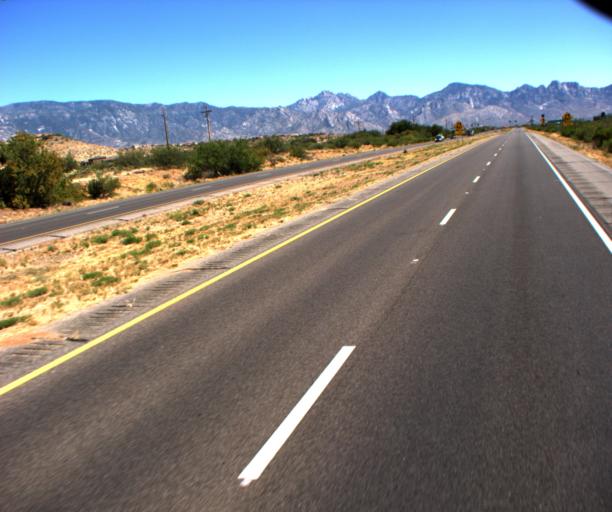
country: US
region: Arizona
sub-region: Pima County
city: Catalina
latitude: 32.5275
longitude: -110.9290
